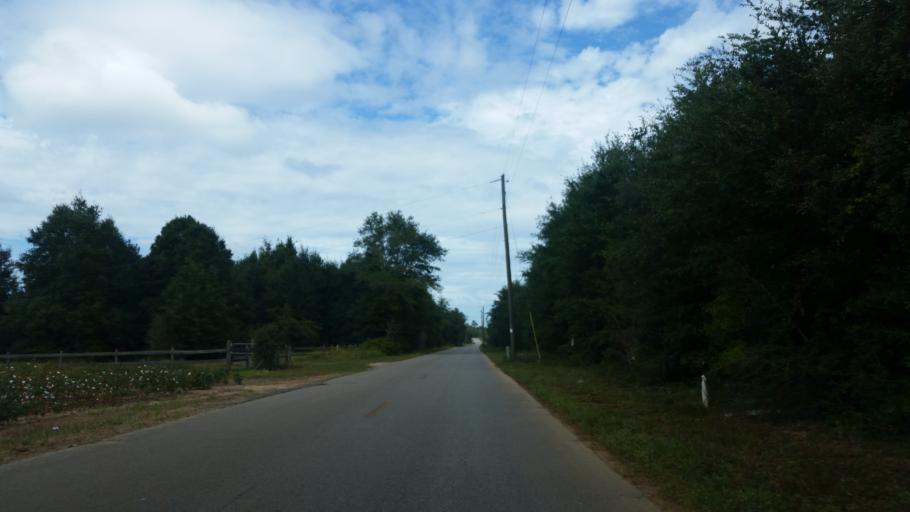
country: US
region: Florida
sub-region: Santa Rosa County
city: Point Baker
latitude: 30.7230
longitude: -86.9927
